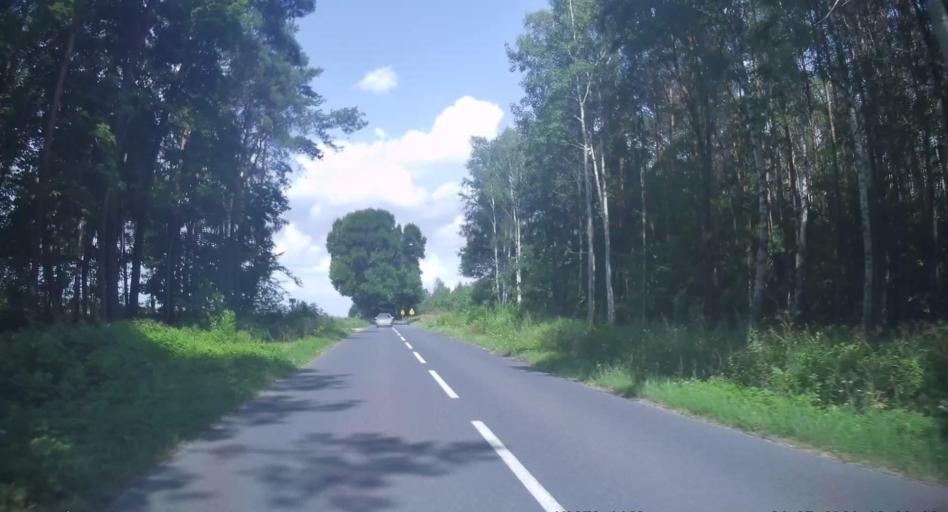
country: PL
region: Lodz Voivodeship
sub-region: Powiat tomaszowski
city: Lubochnia
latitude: 51.5608
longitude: 20.1262
